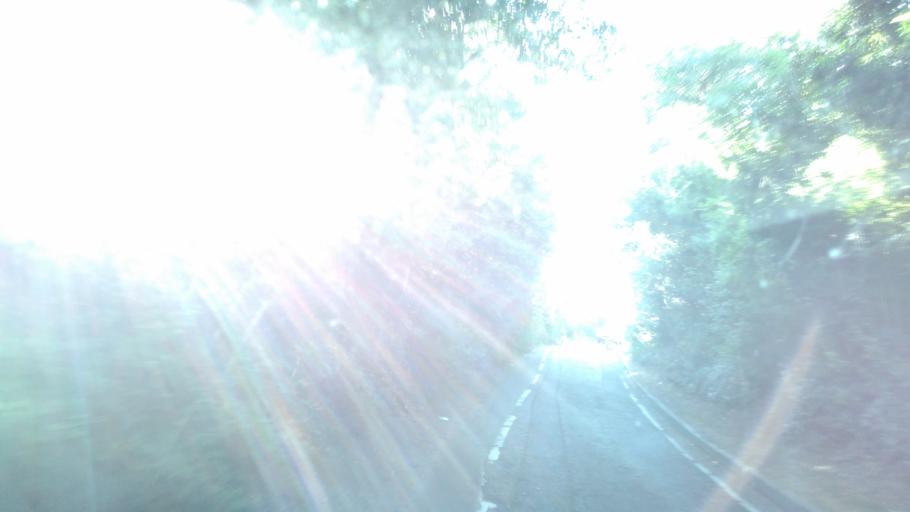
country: GB
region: England
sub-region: Kent
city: Whitstable
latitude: 51.3418
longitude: 1.0050
